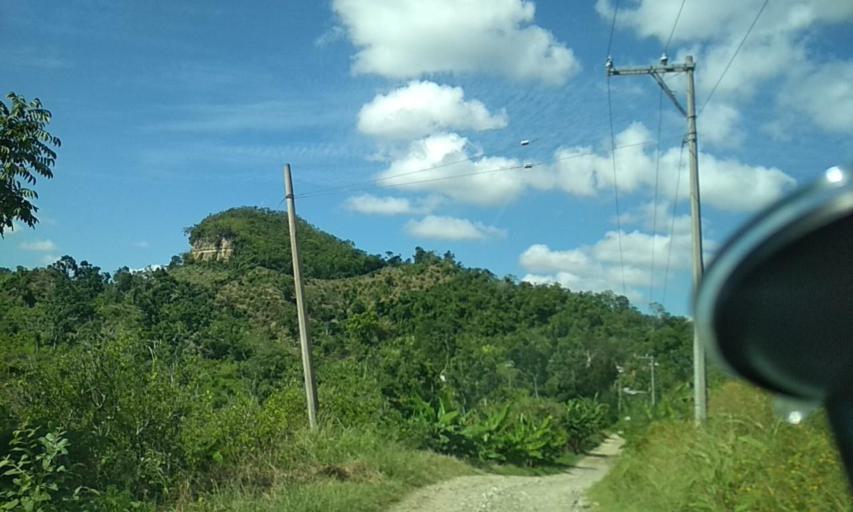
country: MX
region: Veracruz
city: Cazones de Herrera
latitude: 20.6223
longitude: -97.3243
